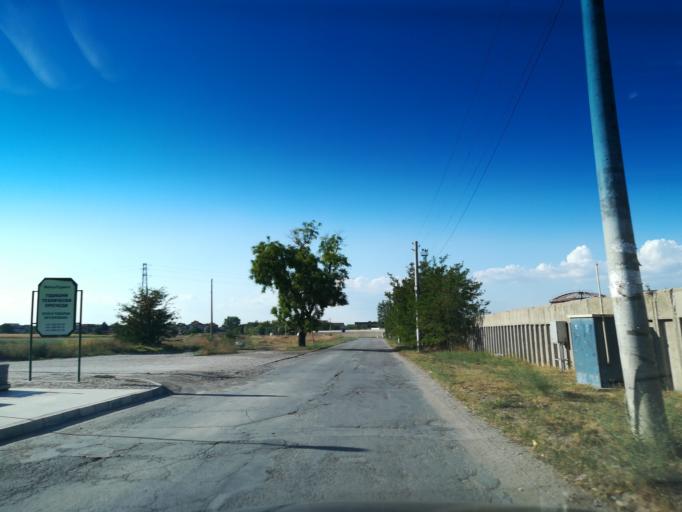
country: BG
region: Stara Zagora
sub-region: Obshtina Chirpan
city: Chirpan
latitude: 42.0910
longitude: 25.2374
